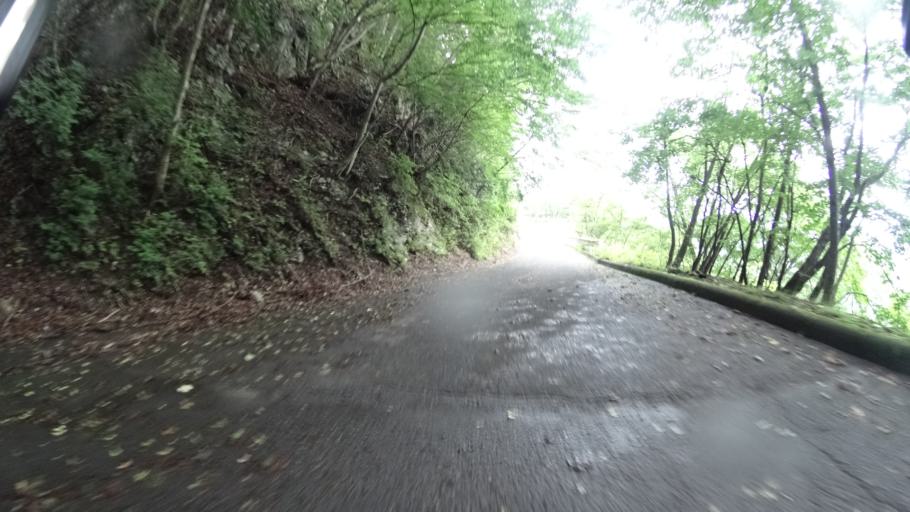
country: JP
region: Saitama
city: Chichibu
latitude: 35.8896
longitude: 139.1214
